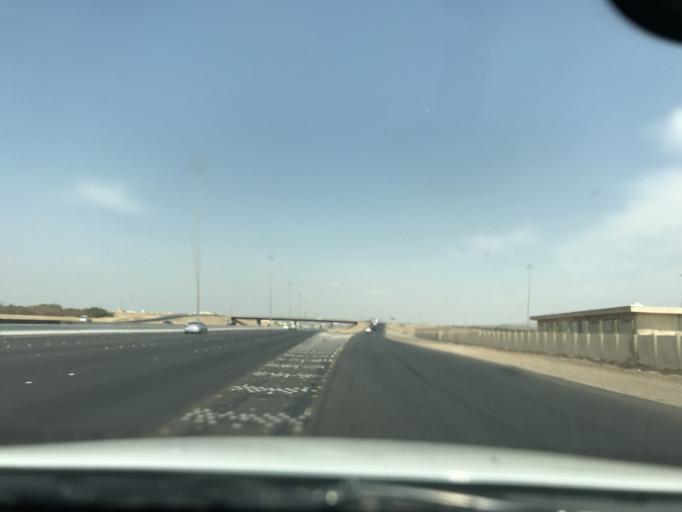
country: SA
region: Makkah
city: Jeddah
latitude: 21.3888
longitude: 39.4217
